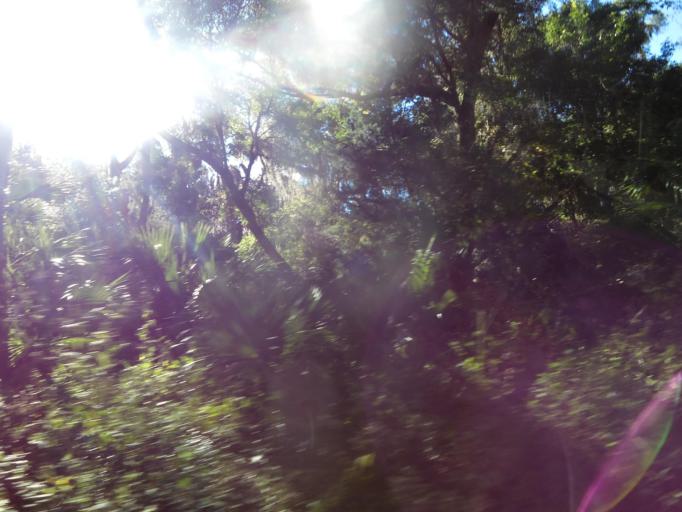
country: US
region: Florida
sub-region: Duval County
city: Atlantic Beach
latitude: 30.4166
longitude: -81.4329
